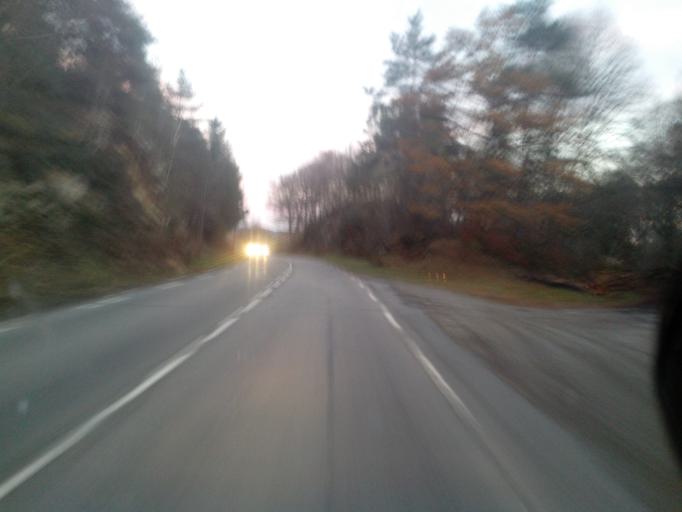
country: FR
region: Limousin
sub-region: Departement de la Correze
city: Meymac
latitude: 45.5126
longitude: 2.1863
